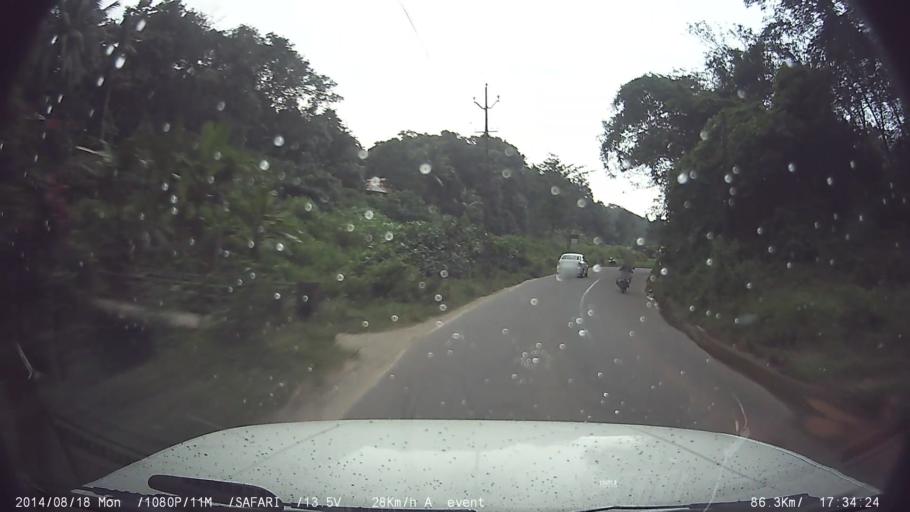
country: IN
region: Kerala
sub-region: Ernakulam
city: Muvattupuzha
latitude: 9.9058
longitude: 76.5846
